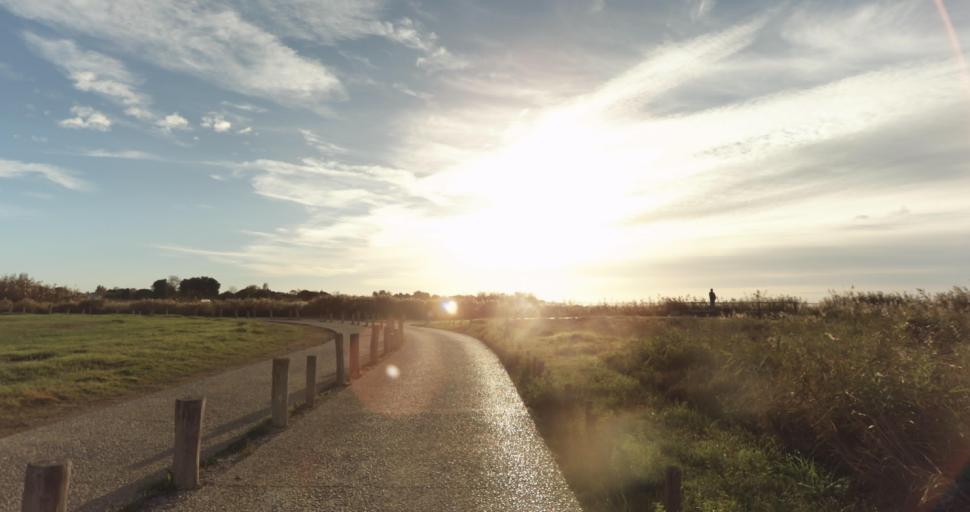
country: FR
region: Languedoc-Roussillon
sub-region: Departement du Gard
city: Aigues-Mortes
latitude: 43.5631
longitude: 4.1921
